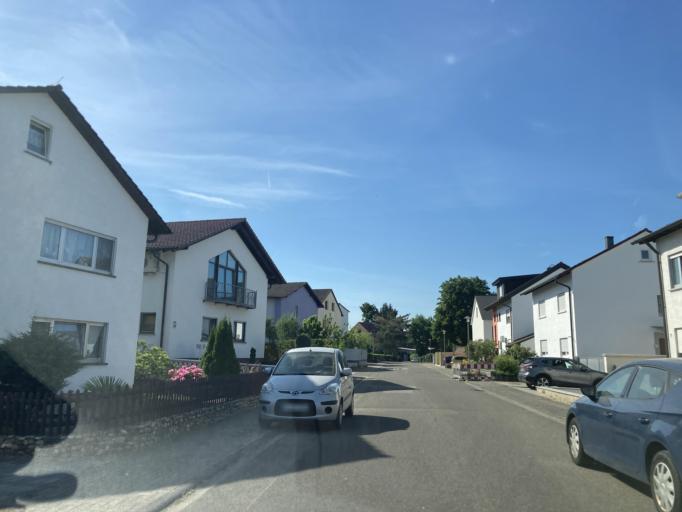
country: DE
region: Baden-Wuerttemberg
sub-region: Karlsruhe Region
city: Kronau
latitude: 49.2029
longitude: 8.6349
